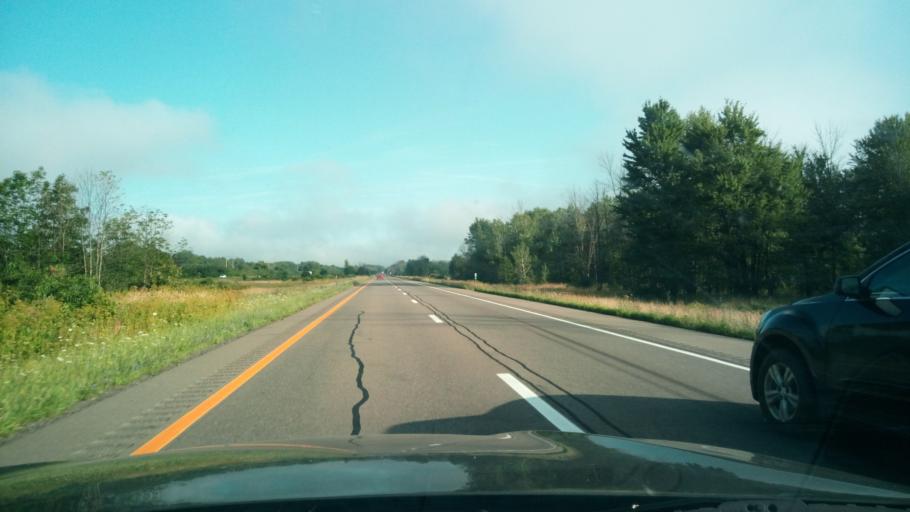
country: US
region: New York
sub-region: Steuben County
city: Bath
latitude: 42.2595
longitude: -77.2115
